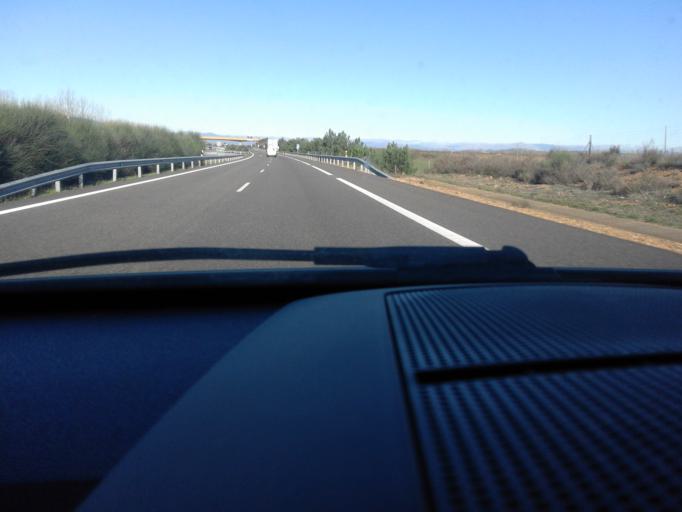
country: ES
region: Castille and Leon
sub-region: Provincia de Leon
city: Vega de Infanzones
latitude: 42.4797
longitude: -5.5512
